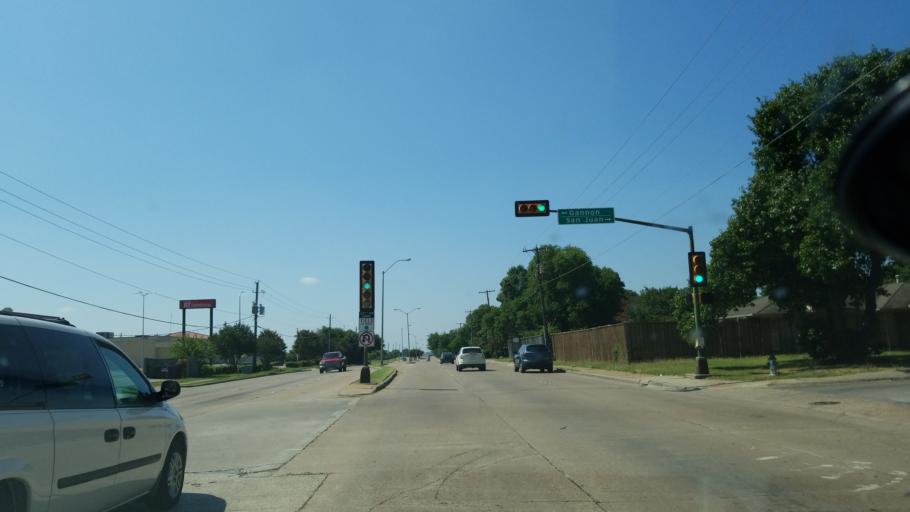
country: US
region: Texas
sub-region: Dallas County
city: Duncanville
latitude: 32.6568
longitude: -96.8914
